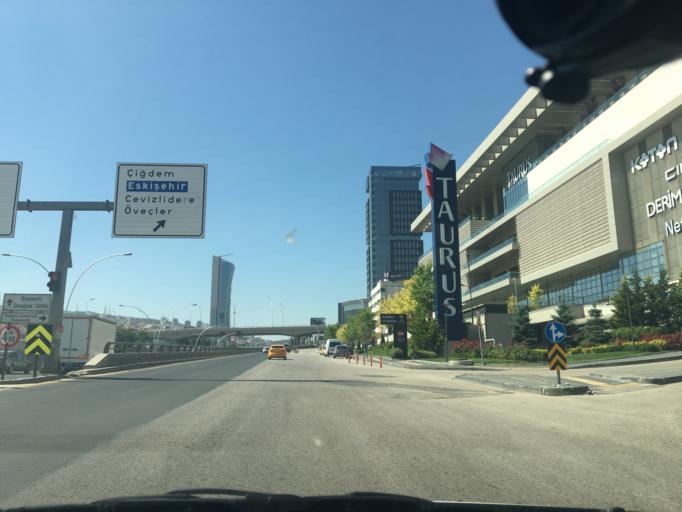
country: TR
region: Ankara
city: Ankara
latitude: 39.8893
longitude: 32.8124
